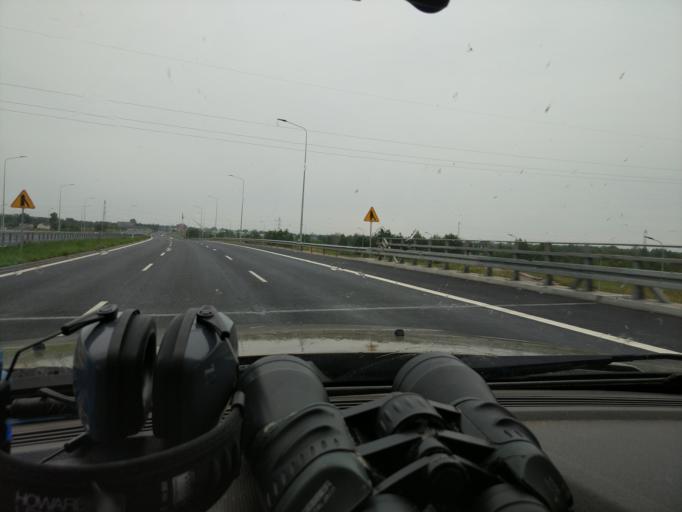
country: PL
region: Masovian Voivodeship
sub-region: Powiat wolominski
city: Radzymin
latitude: 52.3980
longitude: 21.2016
